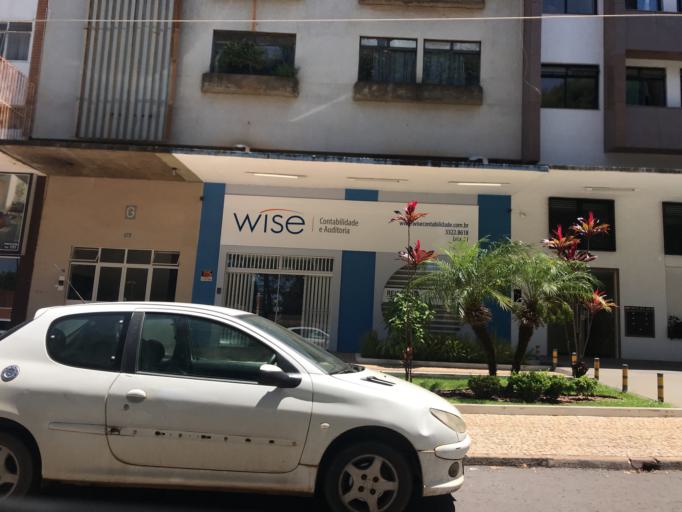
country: BR
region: Federal District
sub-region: Brasilia
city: Brasilia
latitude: -15.7571
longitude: -47.8945
